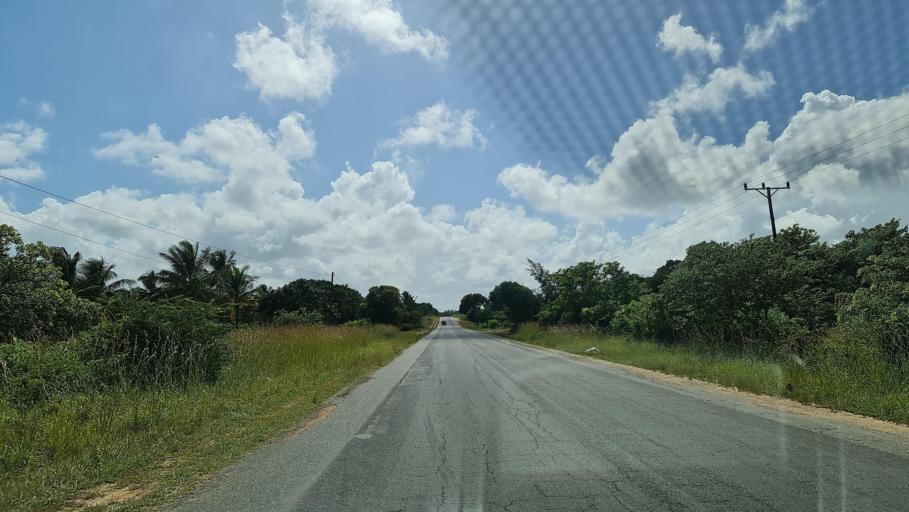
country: MZ
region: Gaza
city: Manjacaze
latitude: -24.6764
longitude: 34.5647
